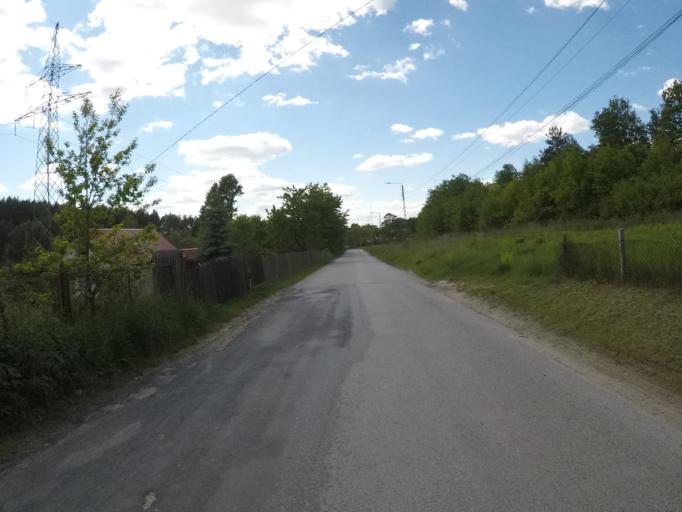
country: PL
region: Swietokrzyskie
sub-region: Powiat kielecki
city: Kostomloty Pierwsze
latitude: 50.9096
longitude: 20.6049
